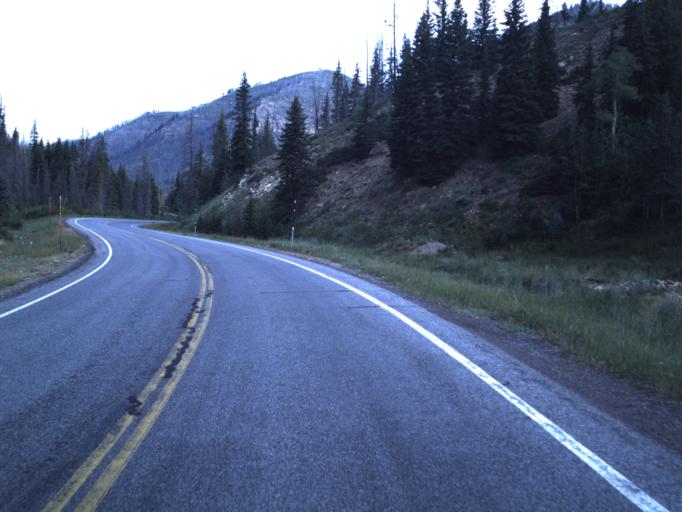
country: US
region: Utah
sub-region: Emery County
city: Huntington
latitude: 39.5249
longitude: -111.1536
